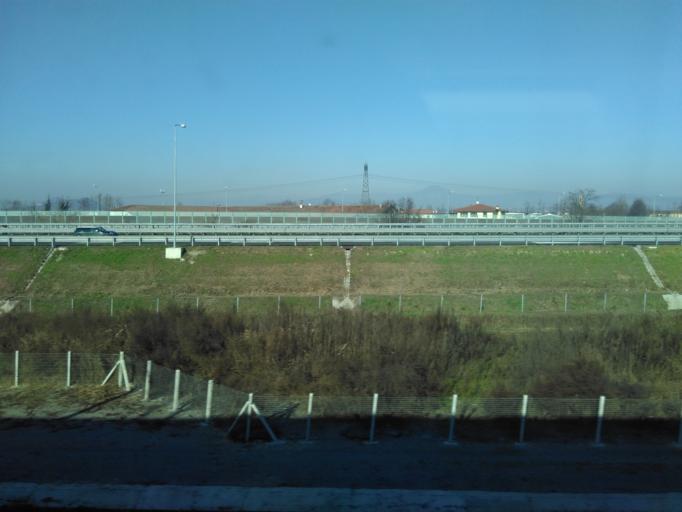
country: IT
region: Lombardy
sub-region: Provincia di Brescia
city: Duomo
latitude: 45.5282
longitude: 10.0437
